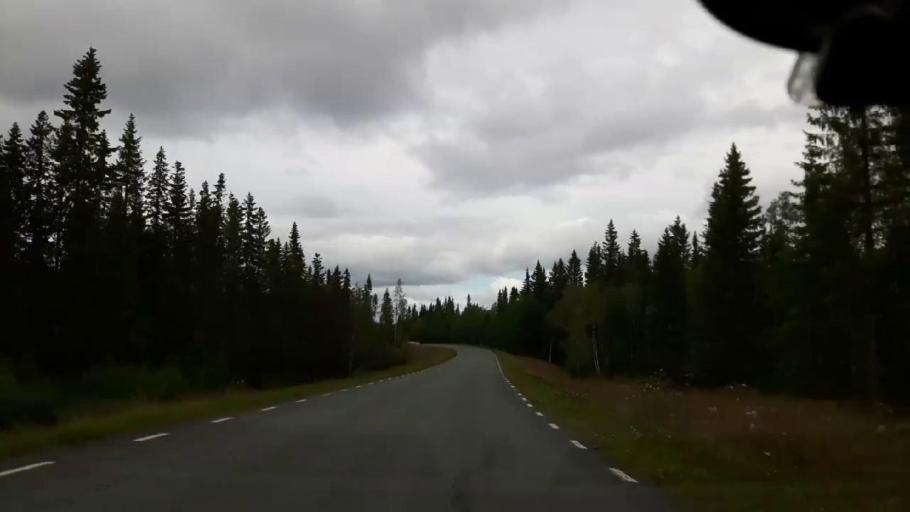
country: SE
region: Jaemtland
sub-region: Krokoms Kommun
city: Valla
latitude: 63.5450
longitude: 13.8536
